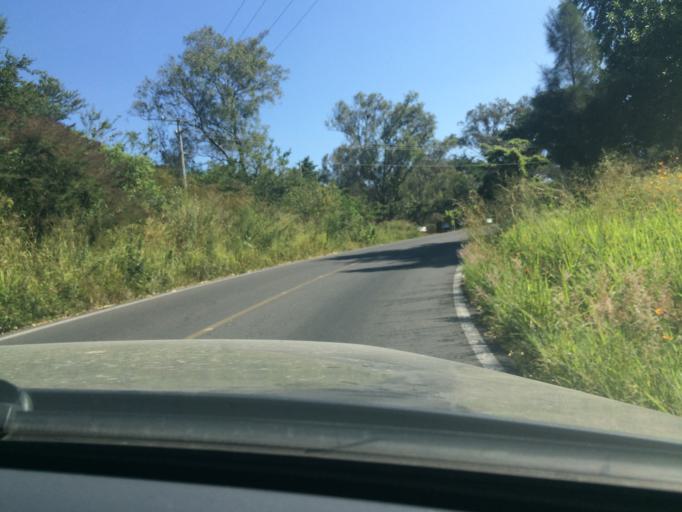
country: MX
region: Colima
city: Suchitlan
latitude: 19.3734
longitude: -103.7215
